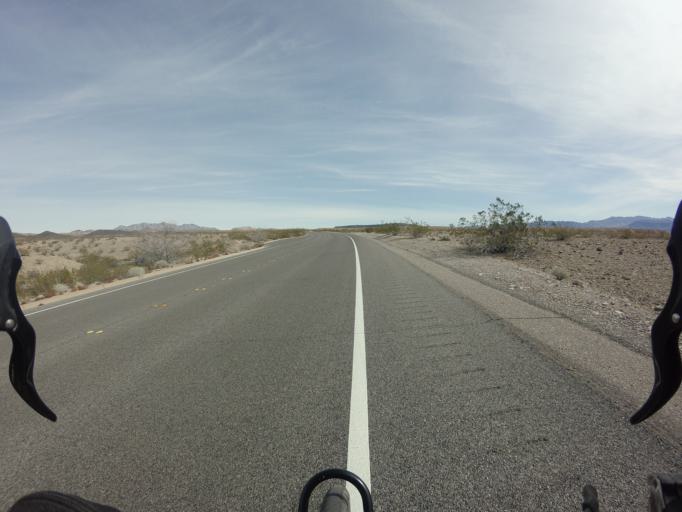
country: US
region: Nevada
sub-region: Clark County
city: Boulder City
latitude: 36.1497
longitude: -114.8398
